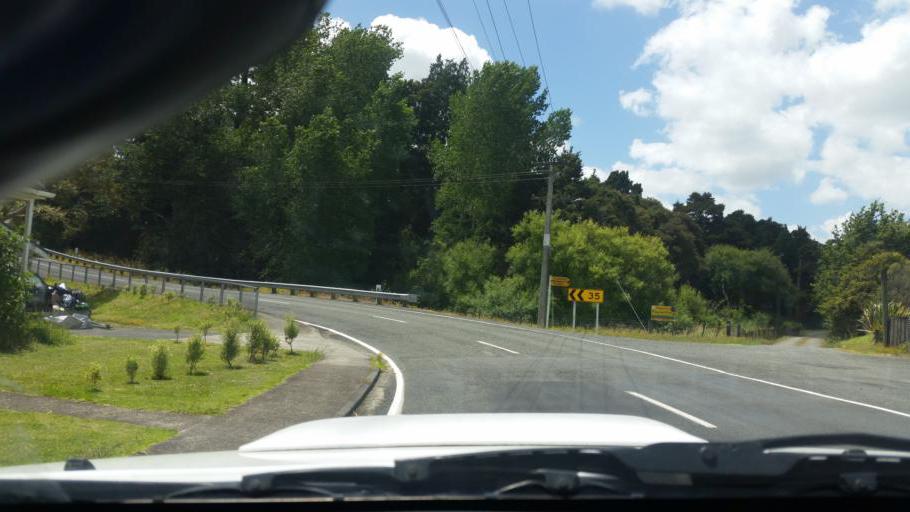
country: NZ
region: Northland
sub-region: Whangarei
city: Ruakaka
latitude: -36.0996
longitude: 174.2331
